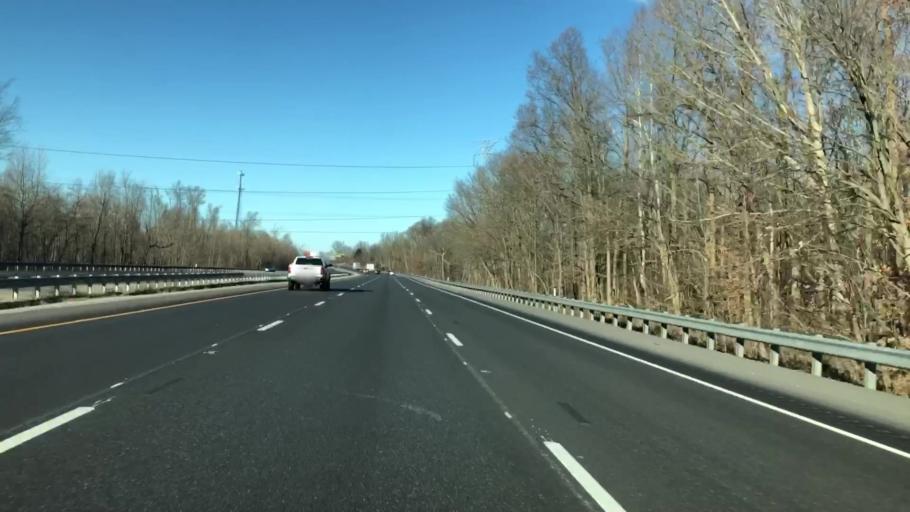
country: US
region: Indiana
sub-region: Clark County
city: Sellersburg
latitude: 38.4328
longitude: -85.7648
